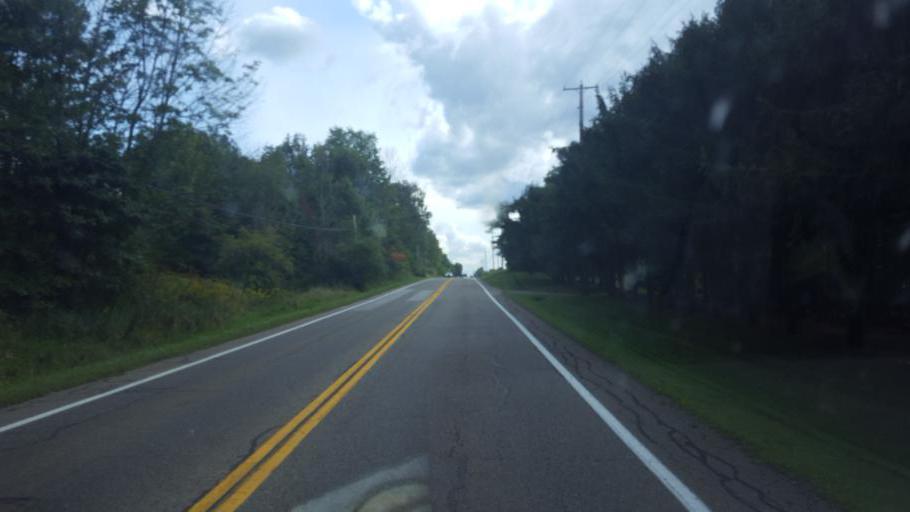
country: US
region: Ohio
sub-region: Portage County
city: Ravenna
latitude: 41.0534
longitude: -81.2477
